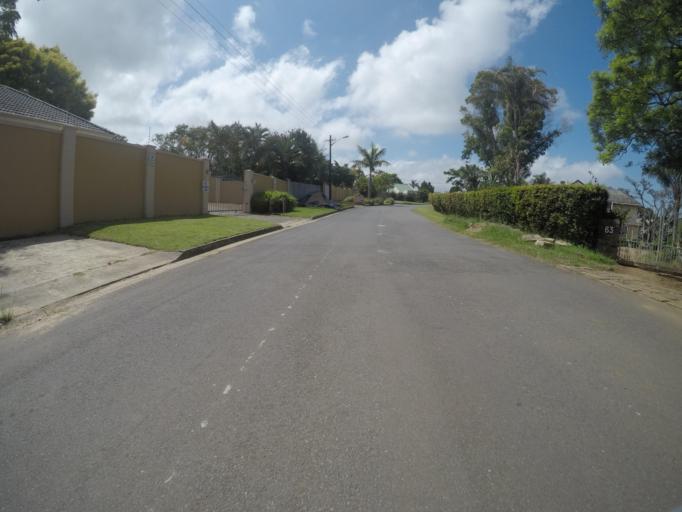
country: ZA
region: Eastern Cape
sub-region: Buffalo City Metropolitan Municipality
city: East London
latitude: -32.9739
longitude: 27.9063
